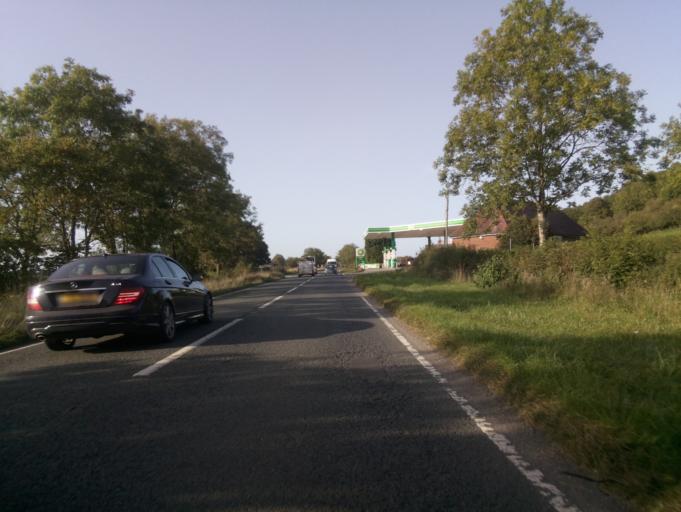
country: GB
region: England
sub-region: Gloucestershire
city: Gloucester
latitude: 51.9371
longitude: -2.2956
